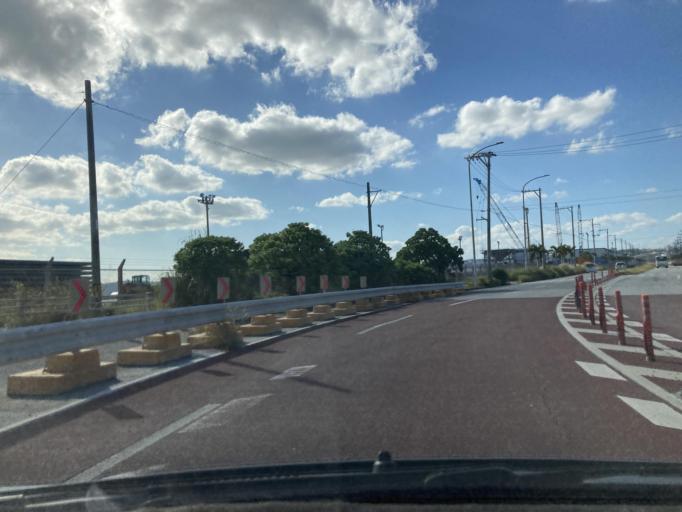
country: JP
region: Okinawa
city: Katsuren-haebaru
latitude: 26.3253
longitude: 127.8539
